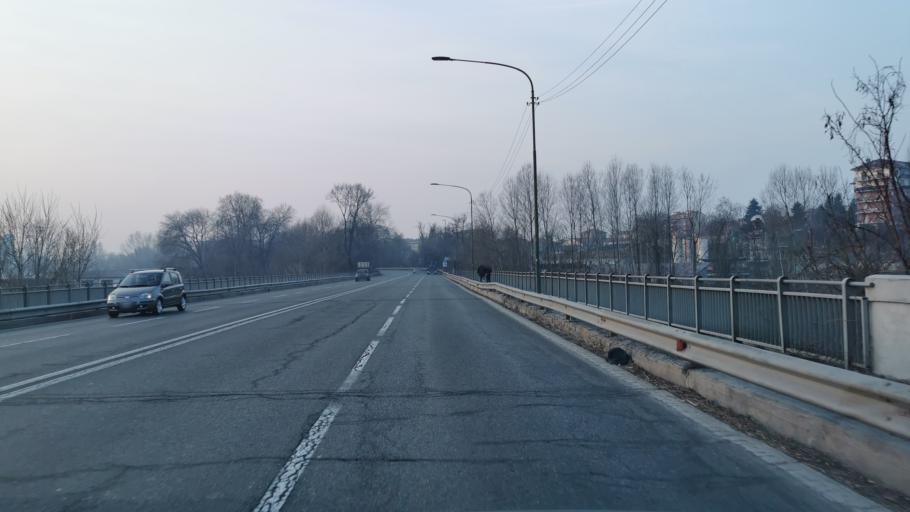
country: IT
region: Piedmont
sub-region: Provincia di Torino
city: Venaria Reale
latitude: 45.1206
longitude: 7.6612
